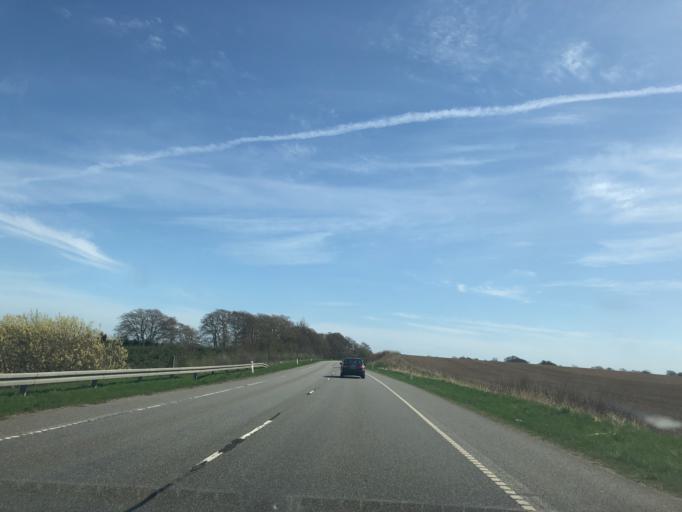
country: DK
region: Zealand
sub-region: Faxe Kommune
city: Haslev
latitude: 55.3057
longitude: 11.9879
